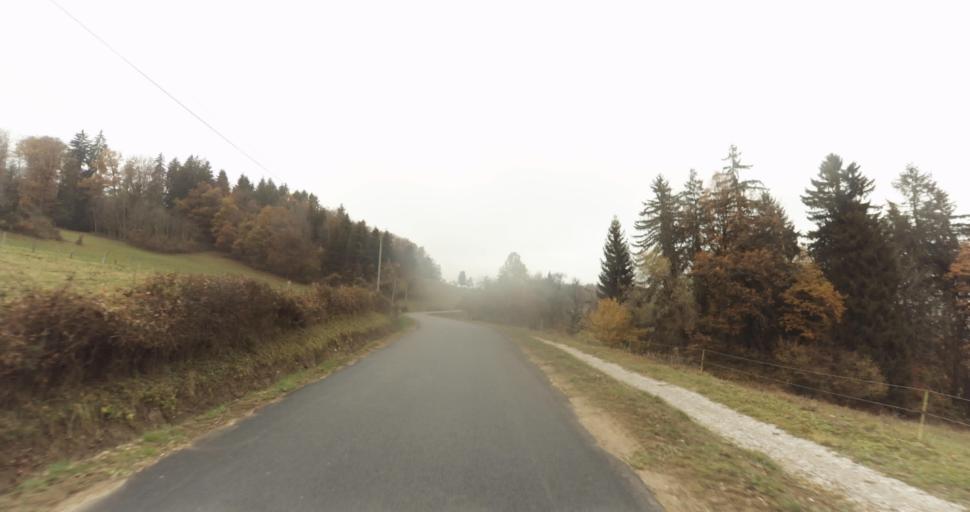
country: FR
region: Rhone-Alpes
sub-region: Departement de la Haute-Savoie
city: Saint-Martin-Bellevue
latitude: 45.9855
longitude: 6.1506
